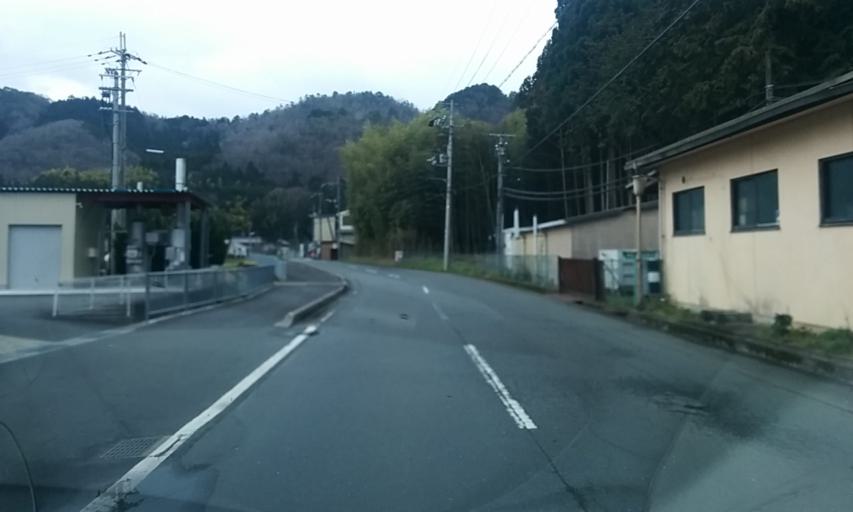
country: JP
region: Kyoto
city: Kameoka
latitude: 35.1402
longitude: 135.4221
